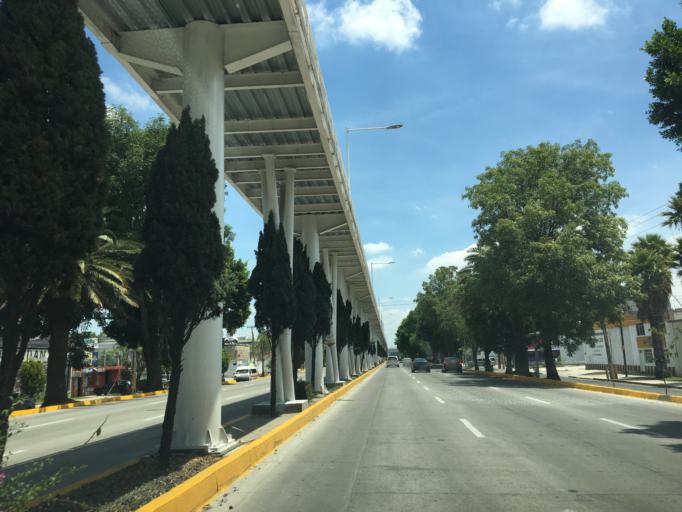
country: MX
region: Puebla
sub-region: Cuautlancingo
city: Sanctorum
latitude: 19.0866
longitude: -98.2290
